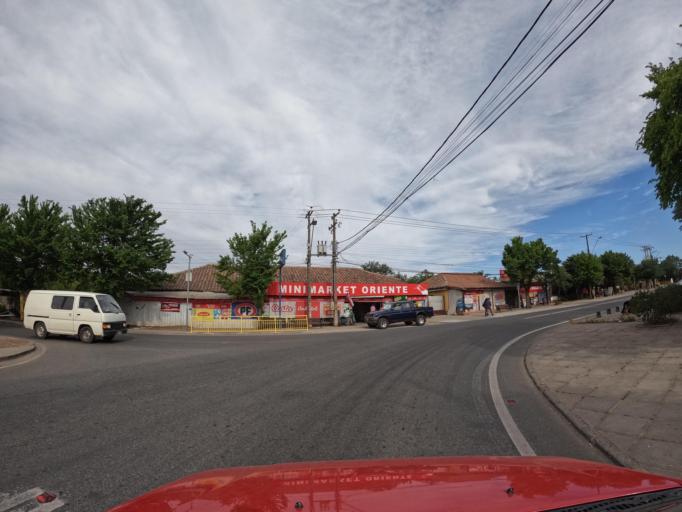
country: CL
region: Maule
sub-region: Provincia de Talca
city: Talca
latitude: -35.3961
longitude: -71.7990
